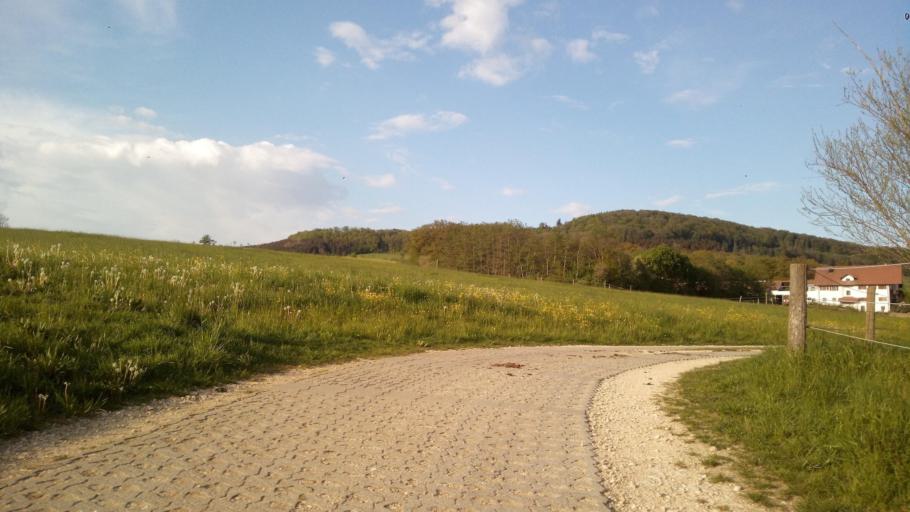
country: DE
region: Baden-Wuerttemberg
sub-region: Regierungsbezirk Stuttgart
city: Salach
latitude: 48.7045
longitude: 9.7470
